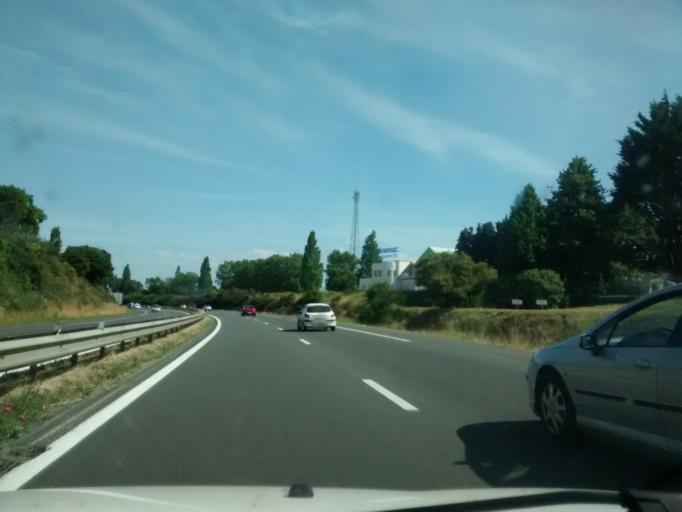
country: FR
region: Brittany
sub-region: Departement des Cotes-d'Armor
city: Langueux
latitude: 48.4891
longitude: -2.7211
